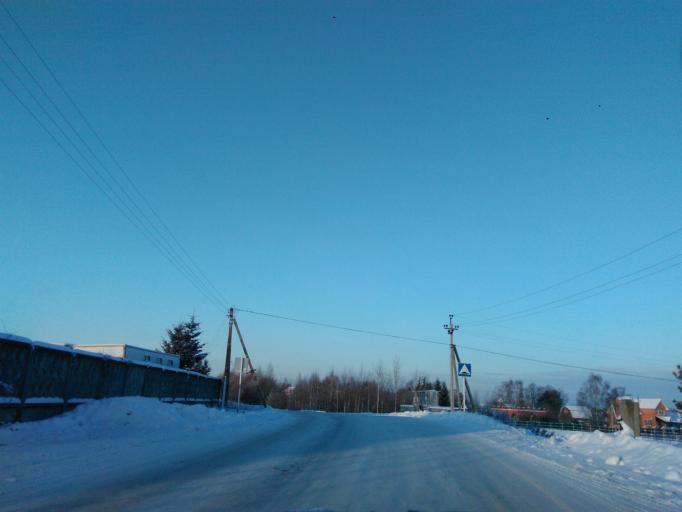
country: RU
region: Tverskaya
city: Zavidovo
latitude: 56.6089
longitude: 36.5692
